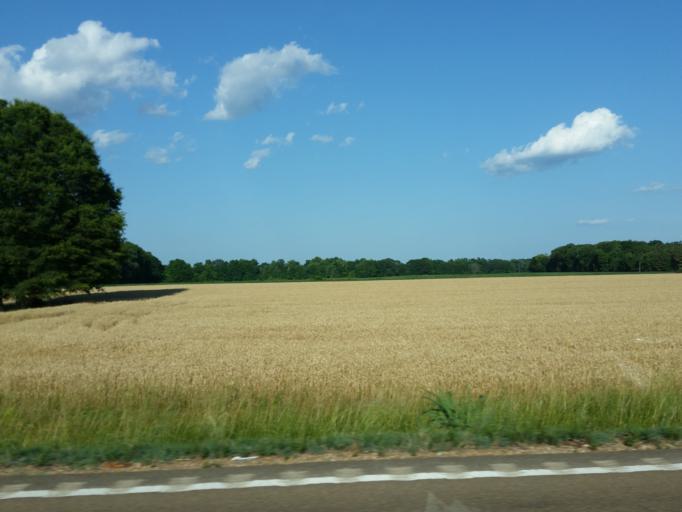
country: US
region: Mississippi
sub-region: Calhoun County
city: Calhoun City
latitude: 33.7641
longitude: -89.3636
